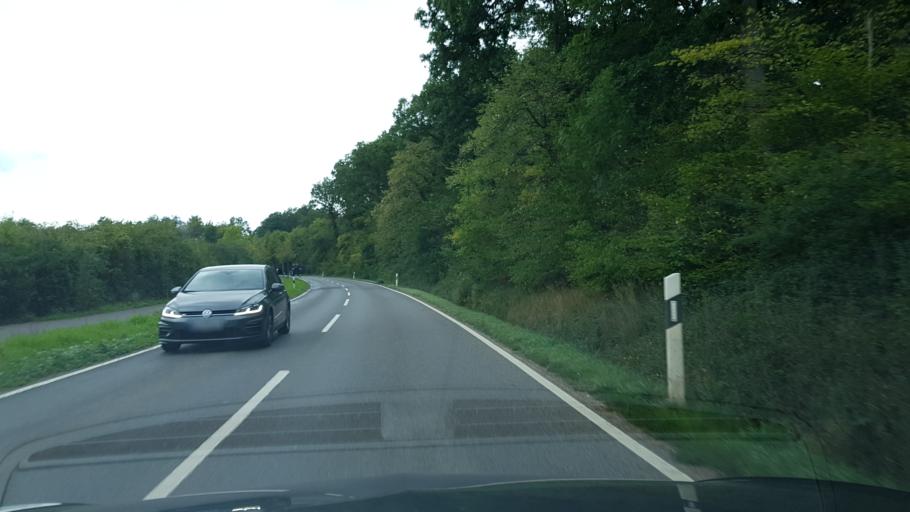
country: DE
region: North Rhine-Westphalia
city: Meckenheim
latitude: 50.6146
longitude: 7.0470
